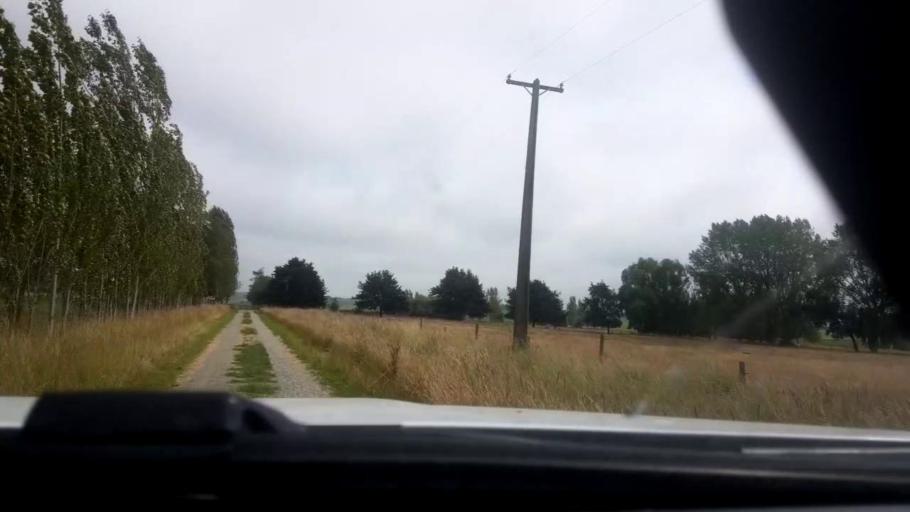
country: NZ
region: Canterbury
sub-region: Timaru District
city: Pleasant Point
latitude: -44.3242
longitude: 171.1941
